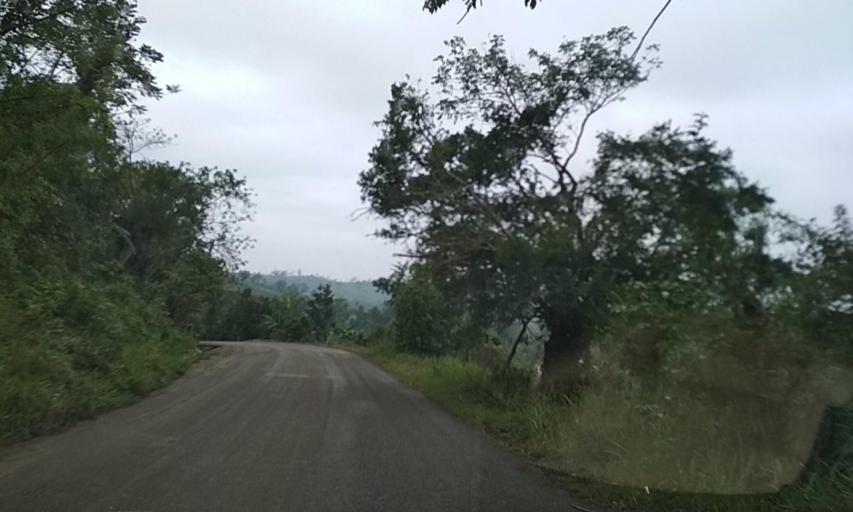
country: MX
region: Veracruz
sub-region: Coatzintla
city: Manuel Maria Contreras
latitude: 20.4494
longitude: -97.4793
